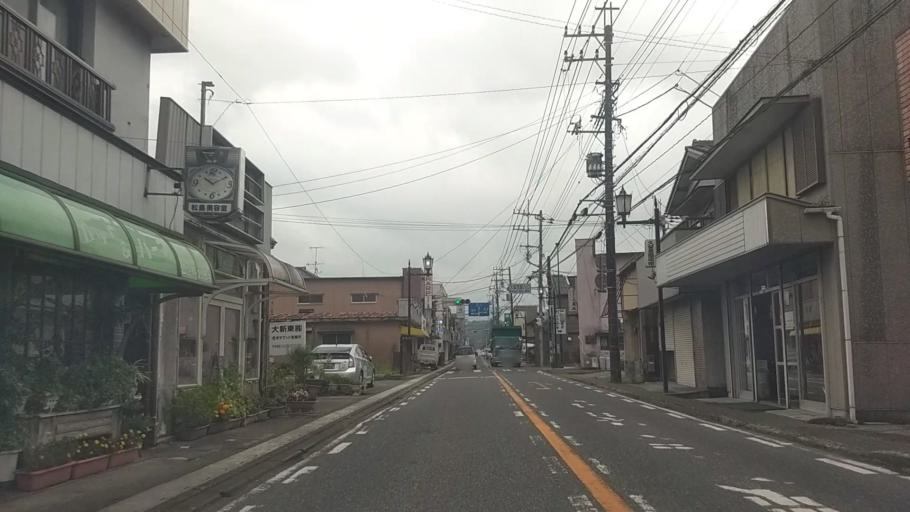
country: JP
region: Chiba
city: Kisarazu
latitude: 35.2968
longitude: 140.0765
